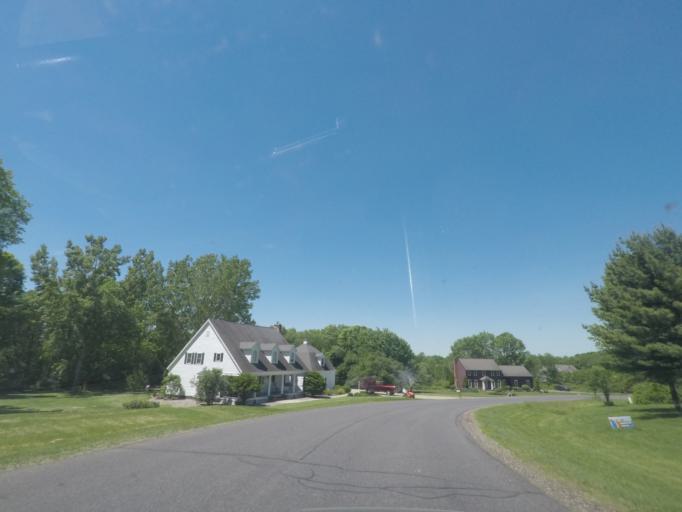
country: US
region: New York
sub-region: Saratoga County
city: Country Knolls
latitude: 42.9398
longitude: -73.7650
